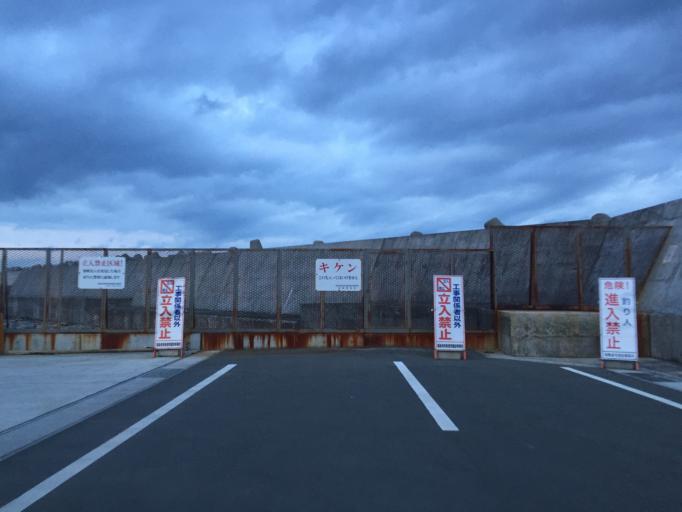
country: JP
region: Miyagi
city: Marumori
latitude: 37.8266
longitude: 140.9817
